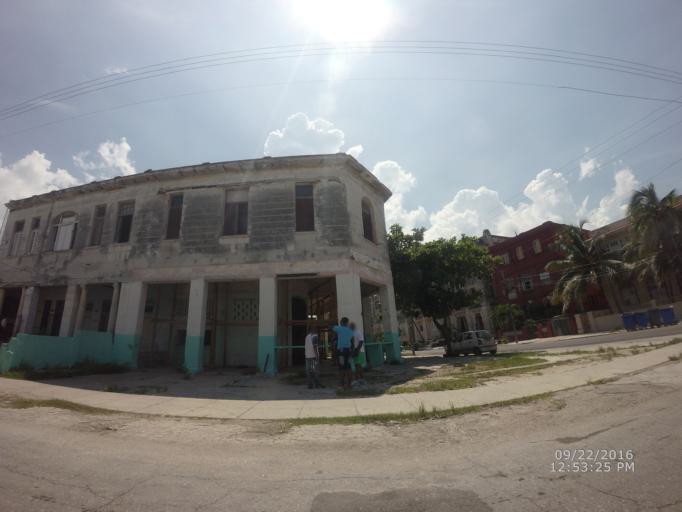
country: CU
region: La Habana
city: Havana
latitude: 23.1450
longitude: -82.3909
